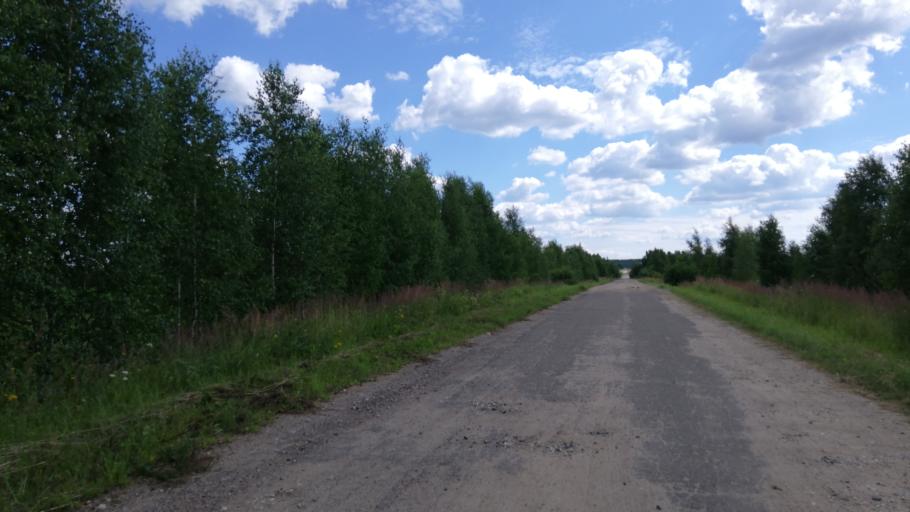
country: RU
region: Jaroslavl
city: Levashevo
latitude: 57.6369
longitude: 40.4635
